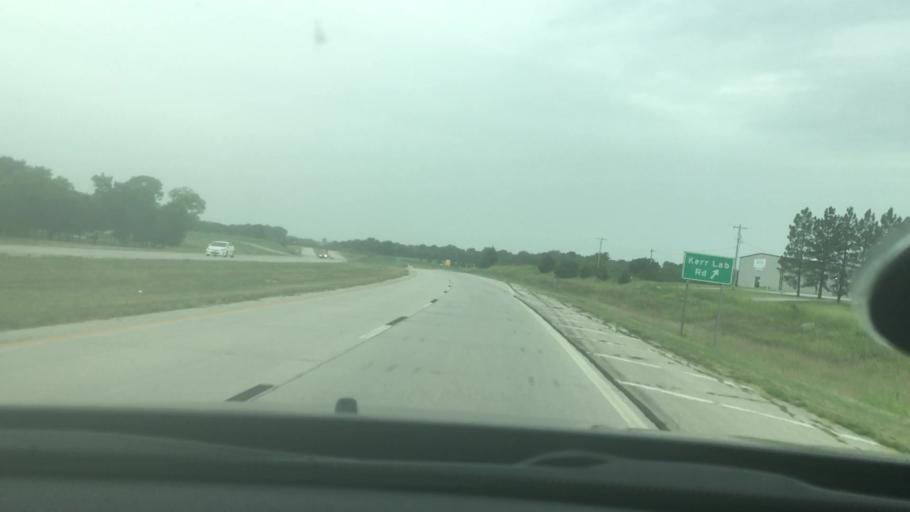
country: US
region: Oklahoma
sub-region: Pontotoc County
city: Ada
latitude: 34.7521
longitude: -96.6633
